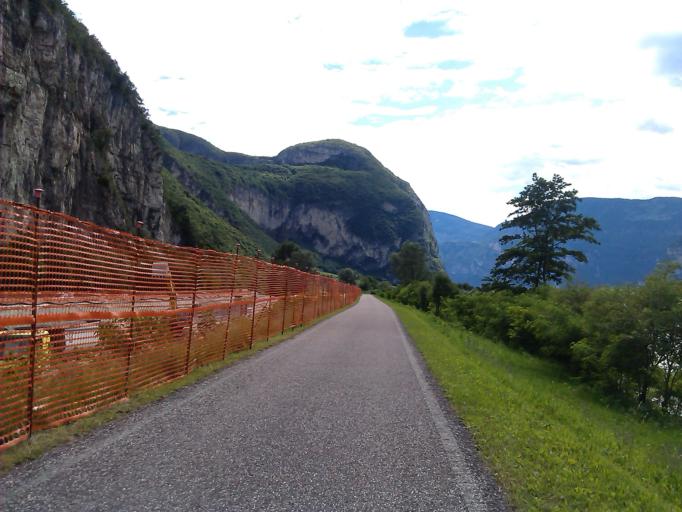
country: IT
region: Trentino-Alto Adige
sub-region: Provincia di Trento
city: Rovere della Luna
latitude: 46.2349
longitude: 11.1810
